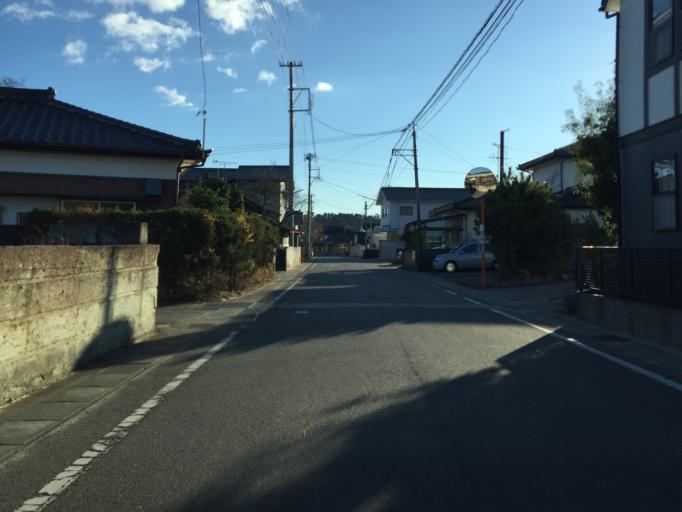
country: JP
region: Fukushima
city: Iwaki
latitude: 37.1303
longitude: 140.8611
